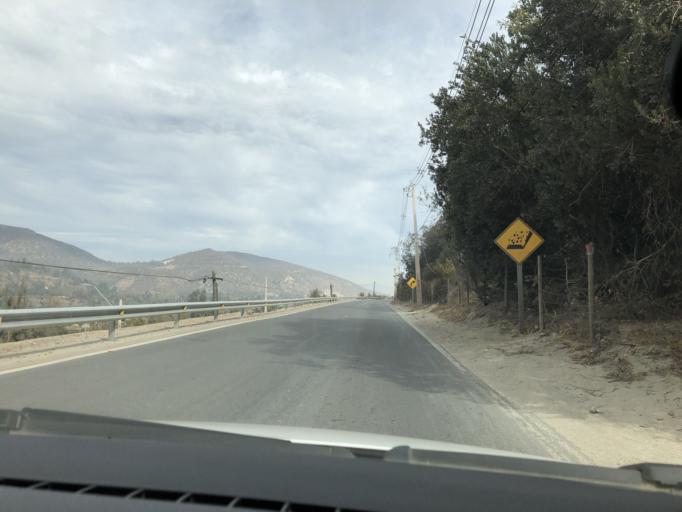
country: CL
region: Santiago Metropolitan
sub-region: Provincia de Cordillera
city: Puente Alto
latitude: -33.5961
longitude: -70.4923
